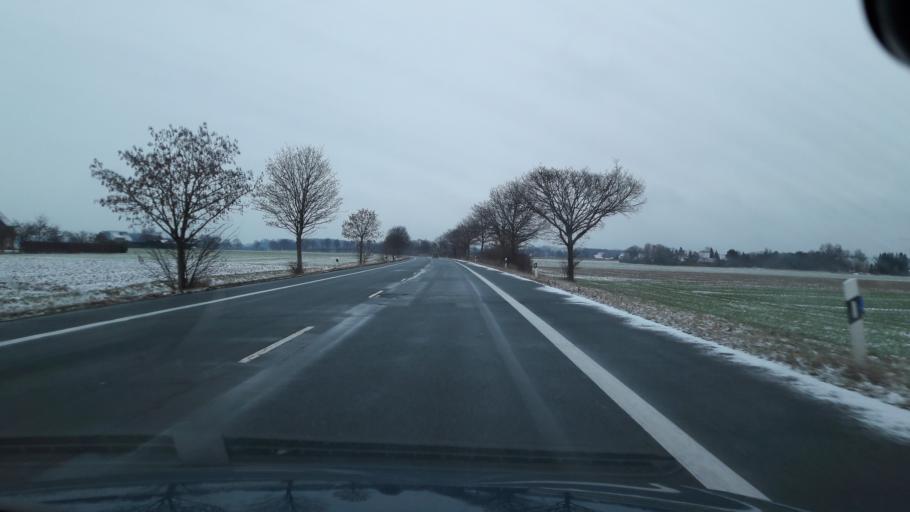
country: DE
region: North Rhine-Westphalia
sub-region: Regierungsbezirk Munster
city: Wadersloh
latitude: 51.7280
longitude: 8.2025
